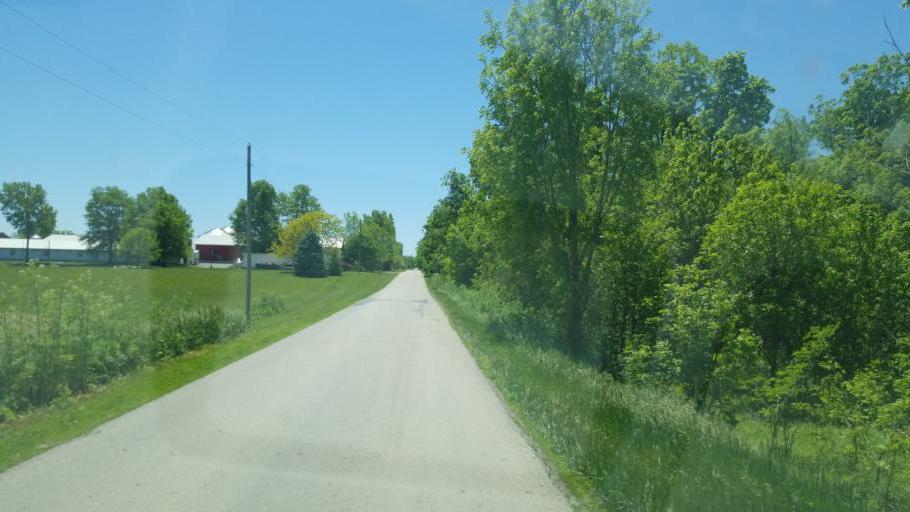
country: US
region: Ohio
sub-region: Mercer County
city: Fort Recovery
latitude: 40.3571
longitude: -84.8040
